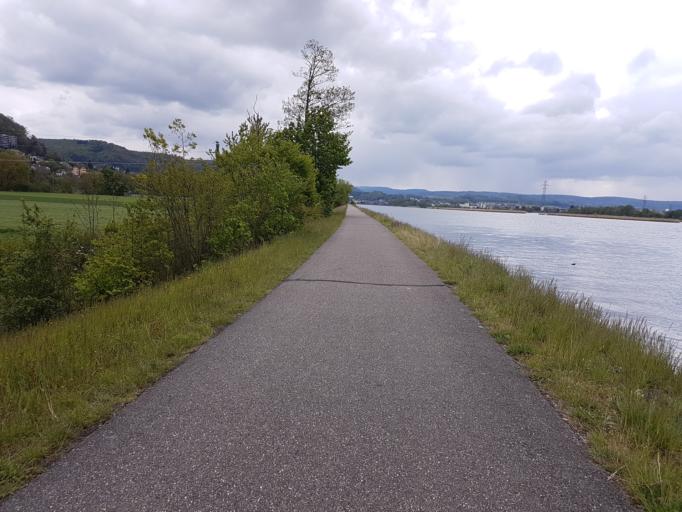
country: CH
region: Aargau
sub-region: Bezirk Zurzach
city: Klingnau
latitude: 47.5889
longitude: 8.2327
